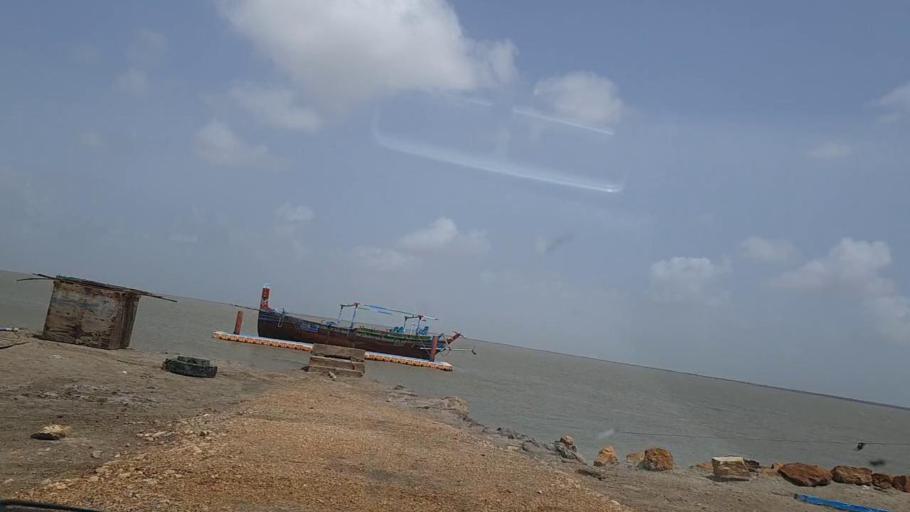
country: PK
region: Sindh
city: Keti Bandar
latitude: 24.1265
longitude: 67.4694
